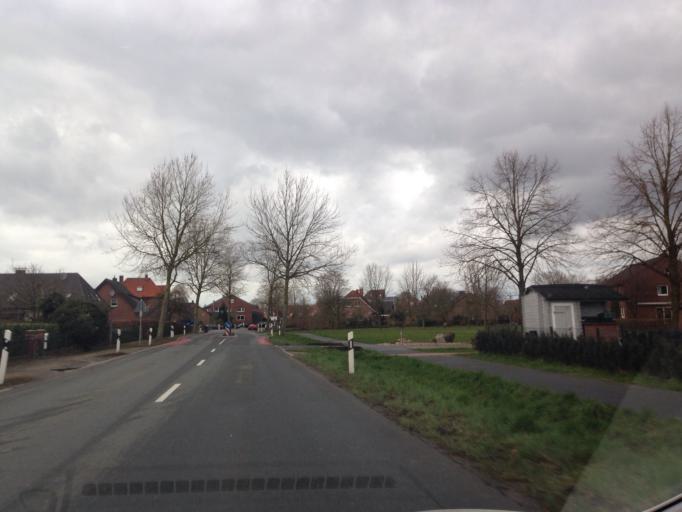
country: DE
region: North Rhine-Westphalia
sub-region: Regierungsbezirk Munster
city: Senden
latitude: 51.8191
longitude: 7.5385
